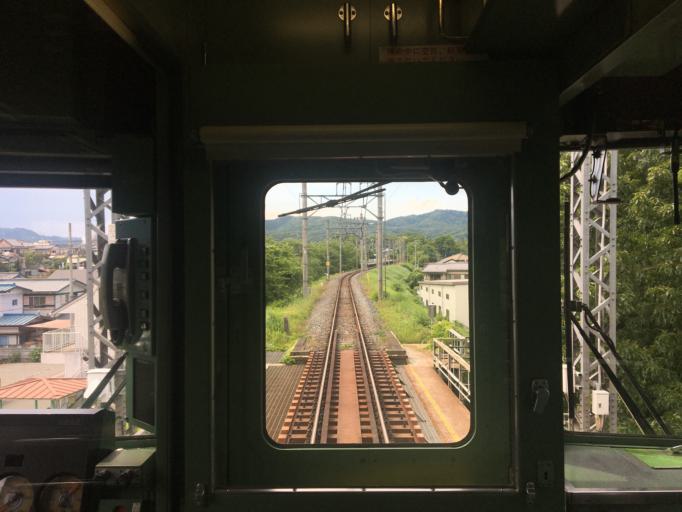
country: JP
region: Saitama
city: Yorii
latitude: 36.1156
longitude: 139.2023
